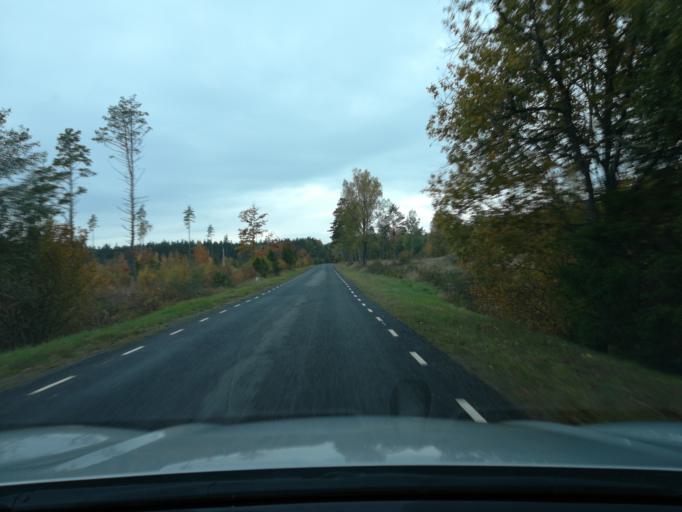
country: EE
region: Ida-Virumaa
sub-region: Johvi vald
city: Johvi
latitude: 59.0223
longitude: 27.4009
